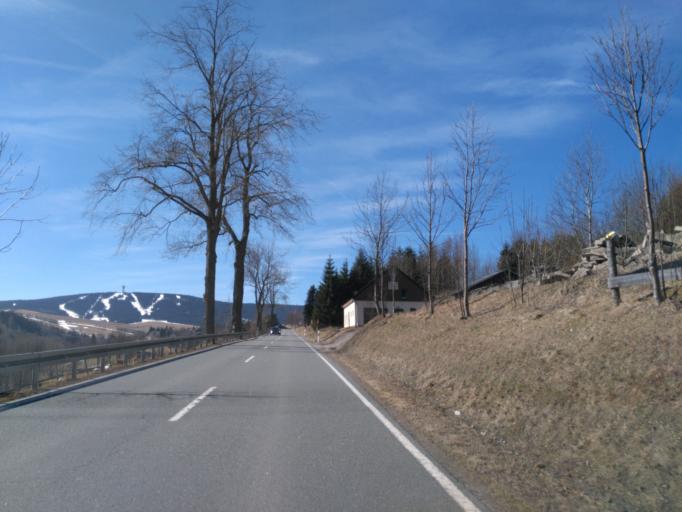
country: DE
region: Saxony
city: Kurort Oberwiesenthal
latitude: 50.4333
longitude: 12.9940
